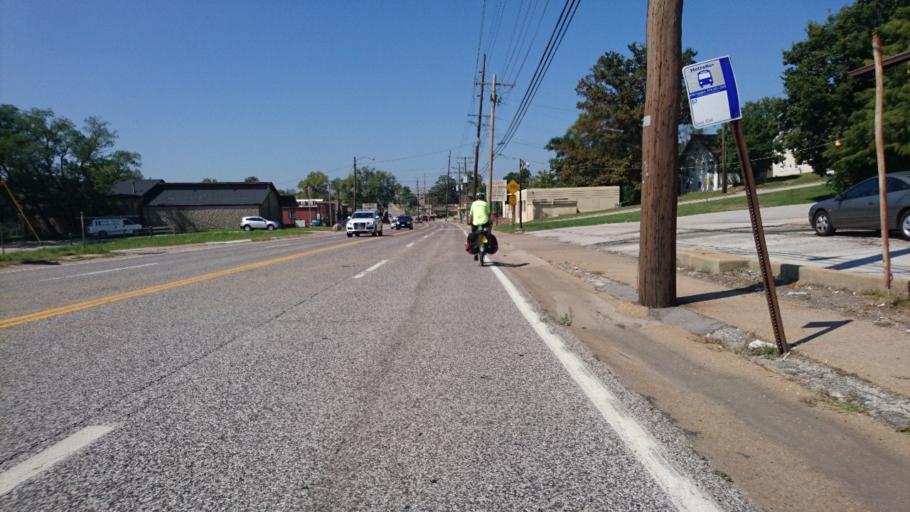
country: US
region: Missouri
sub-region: Saint Louis County
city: Brentwood
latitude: 38.6120
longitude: -90.3408
